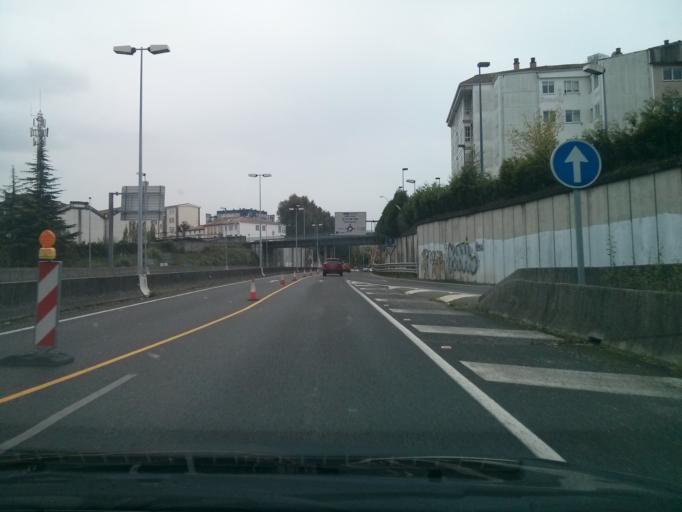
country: ES
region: Galicia
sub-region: Provincia da Coruna
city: Santiago de Compostela
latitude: 42.8671
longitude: -8.5529
